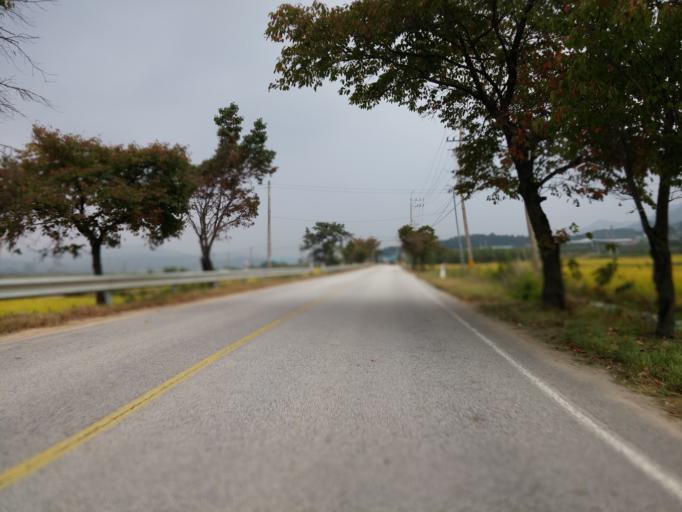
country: KR
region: Chungcheongbuk-do
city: Okcheon
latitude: 36.4023
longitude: 127.7446
